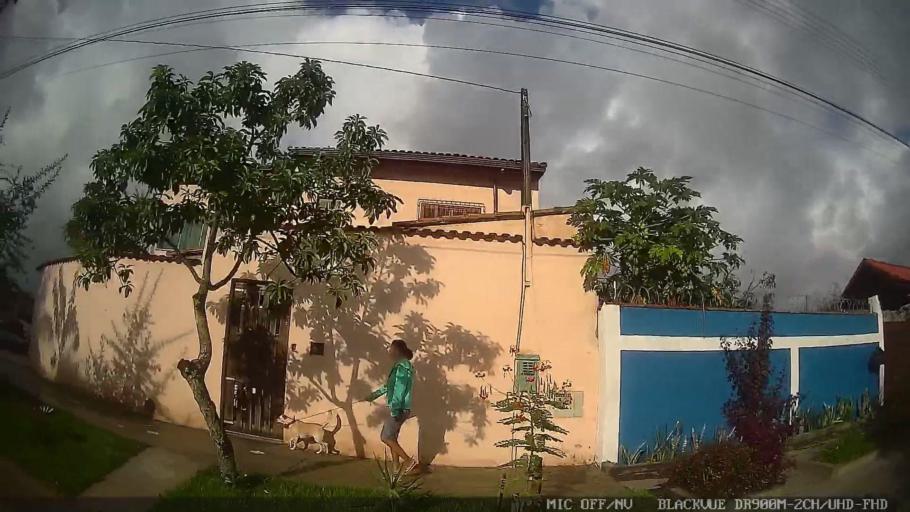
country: BR
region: Sao Paulo
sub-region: Itanhaem
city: Itanhaem
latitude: -24.1963
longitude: -46.8672
